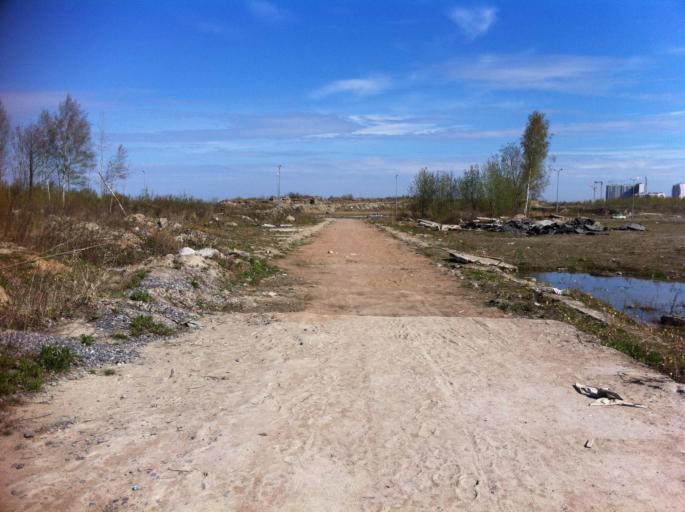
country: RU
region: St.-Petersburg
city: Sosnovaya Polyana
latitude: 59.8561
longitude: 30.1428
